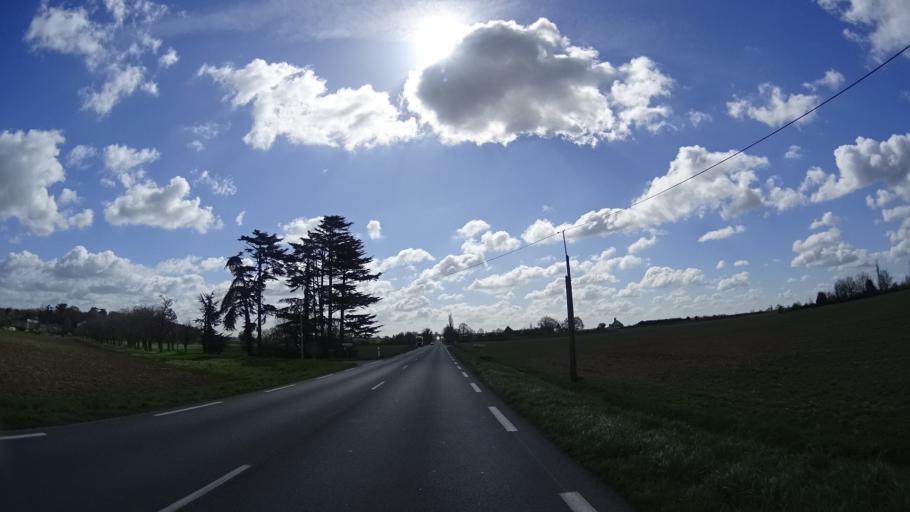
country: FR
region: Pays de la Loire
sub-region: Departement de Maine-et-Loire
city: Brissac-Quince
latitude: 47.3335
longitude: -0.4253
